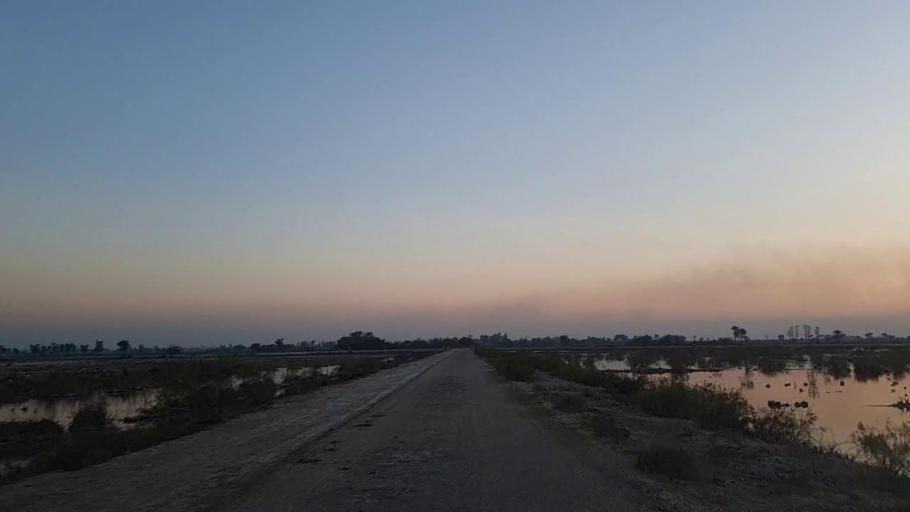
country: PK
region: Sindh
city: Bandhi
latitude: 26.5906
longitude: 68.3359
